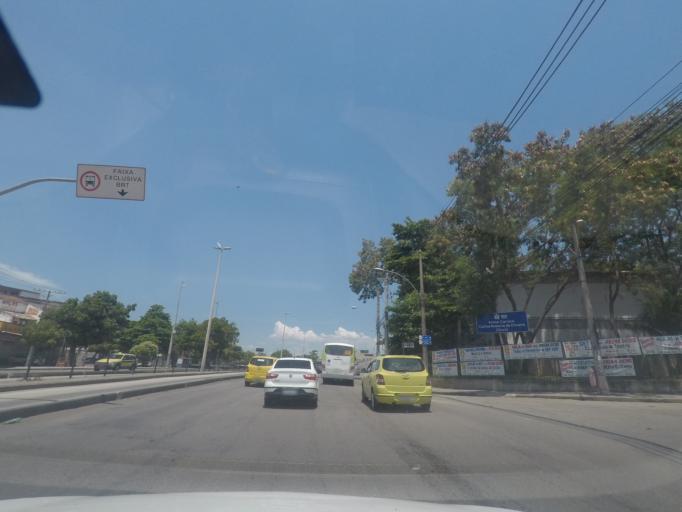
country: BR
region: Rio de Janeiro
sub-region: Duque De Caxias
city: Duque de Caxias
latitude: -22.8378
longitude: -43.2878
